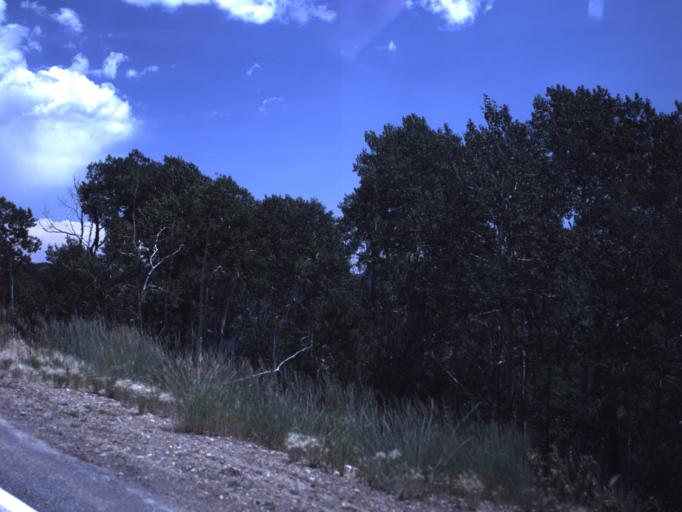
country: US
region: Utah
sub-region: Sanpete County
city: Fairview
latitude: 39.6827
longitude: -111.2114
